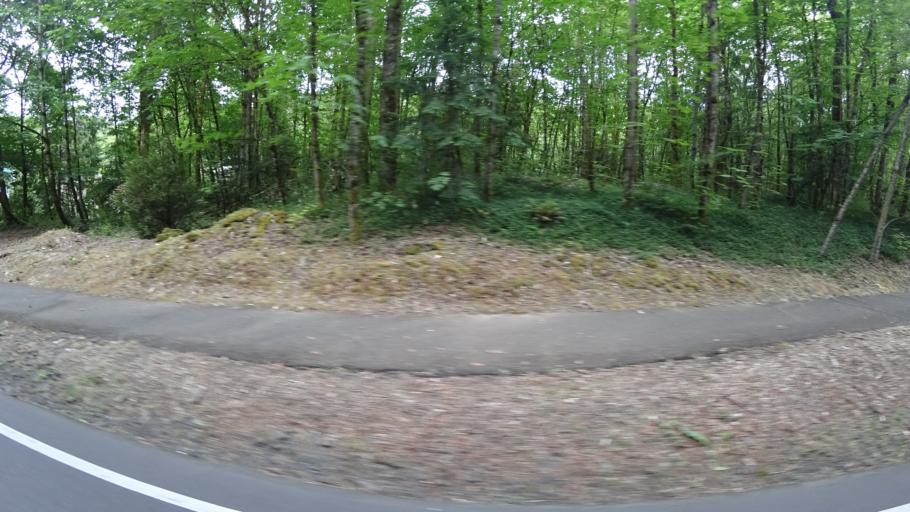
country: US
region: Oregon
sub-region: Clackamas County
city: Lake Oswego
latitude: 45.4279
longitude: -122.7066
